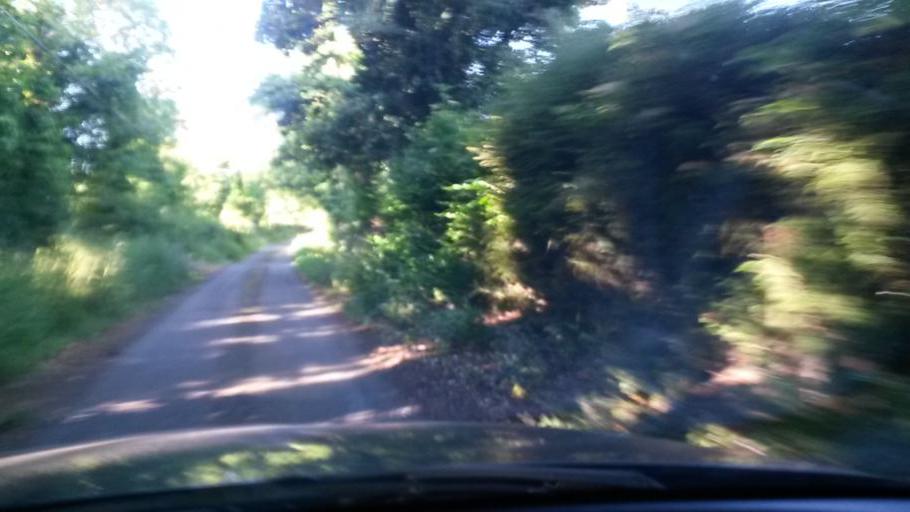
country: IE
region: Leinster
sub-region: Dublin City
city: Finglas
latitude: 53.4353
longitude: -6.3256
